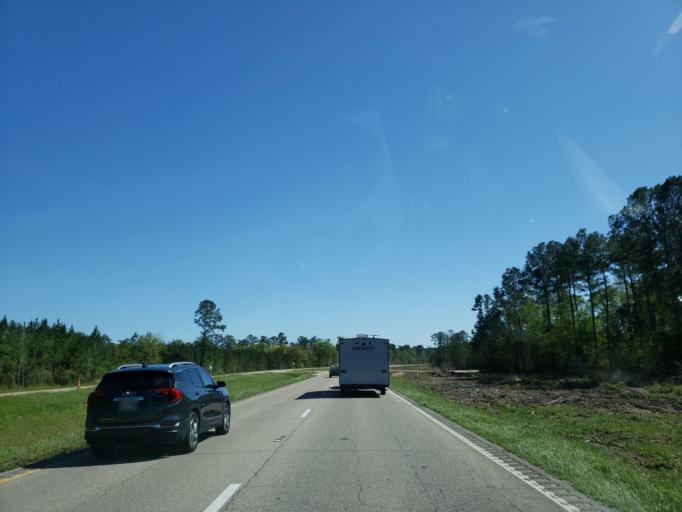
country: US
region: Mississippi
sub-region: Stone County
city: Wiggins
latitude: 31.0502
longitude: -89.2038
